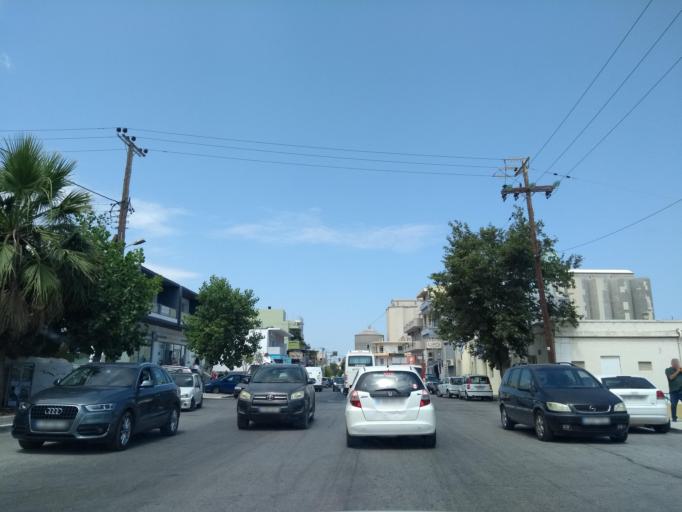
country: GR
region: Crete
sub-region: Nomos Chanias
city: Souda
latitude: 35.4876
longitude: 24.0754
